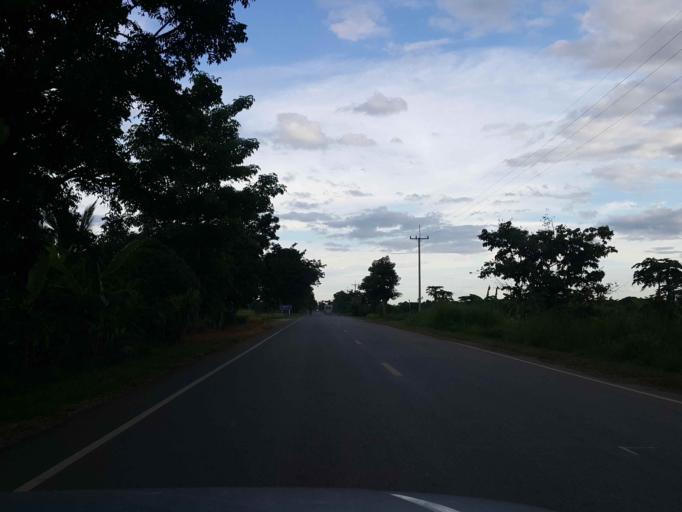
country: TH
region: Sukhothai
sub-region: Amphoe Si Satchanalai
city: Si Satchanalai
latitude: 17.4207
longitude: 99.7259
